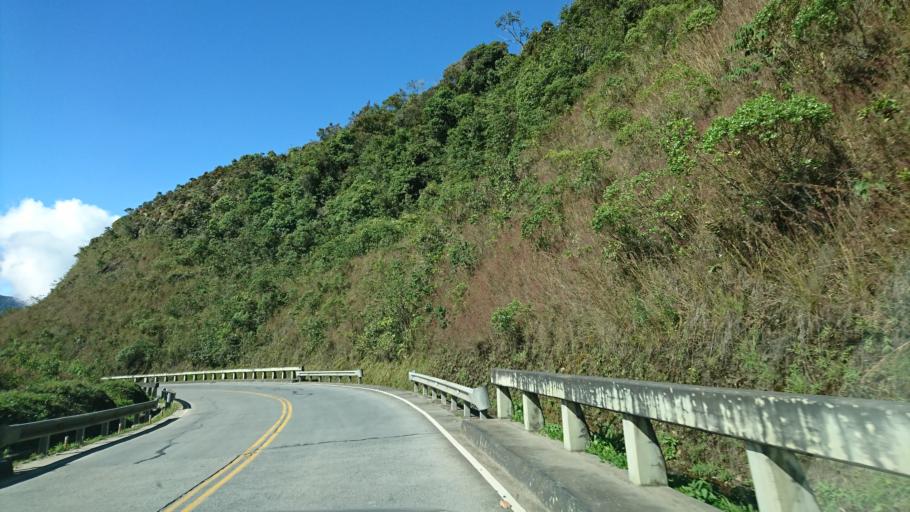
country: BO
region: La Paz
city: Coroico
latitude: -16.2146
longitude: -67.8290
